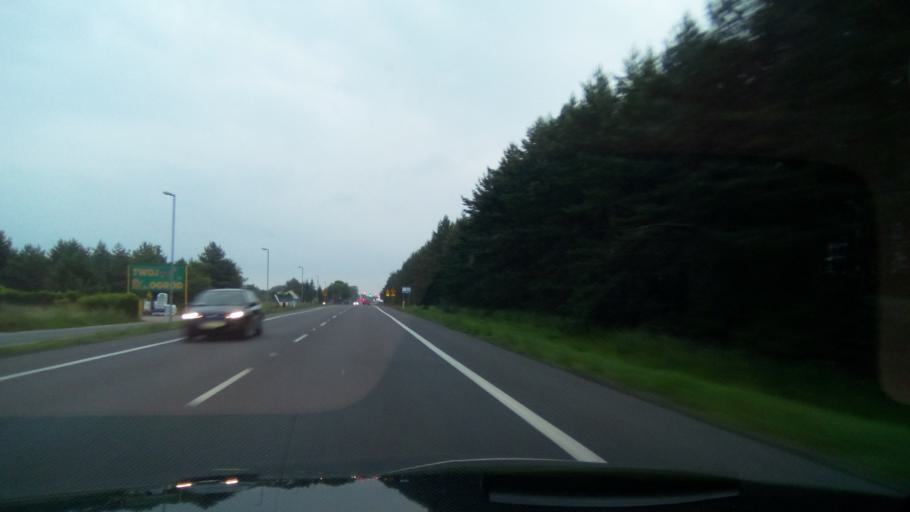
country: PL
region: Greater Poland Voivodeship
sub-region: Powiat poznanski
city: Pobiedziska
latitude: 52.4742
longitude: 17.2325
